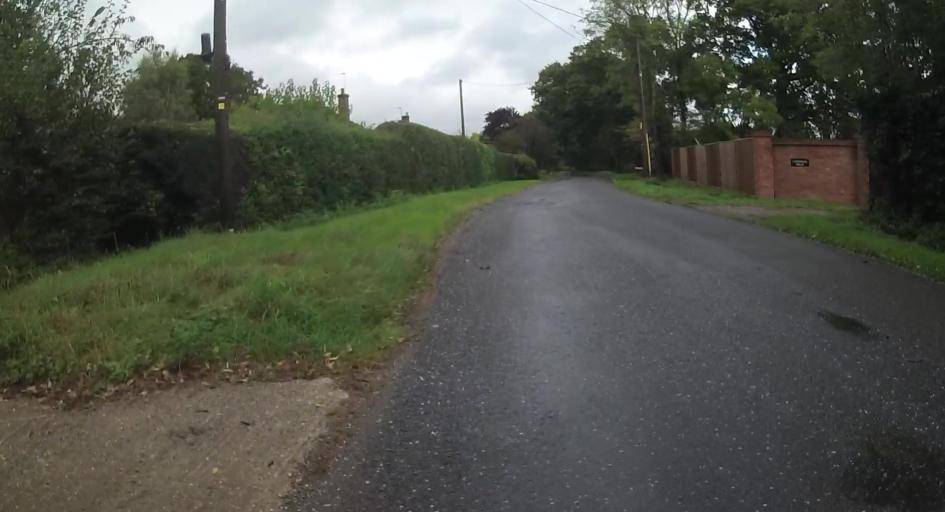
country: GB
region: England
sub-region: Hampshire
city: Tadley
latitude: 51.3201
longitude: -1.1575
